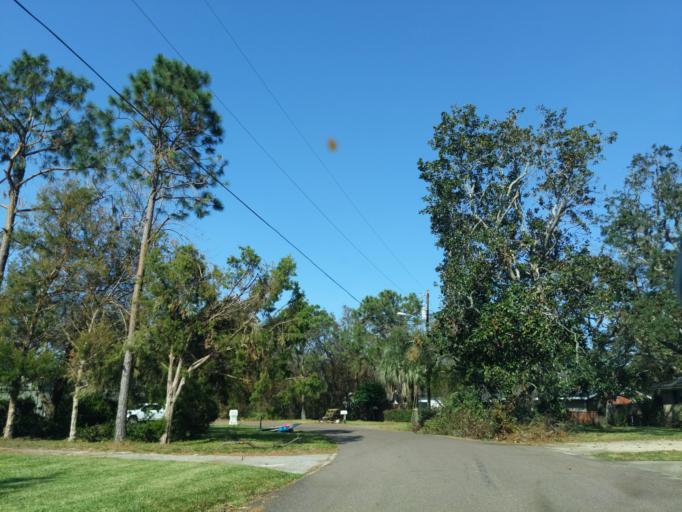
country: US
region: Florida
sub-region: Santa Rosa County
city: Gulf Breeze
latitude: 30.3599
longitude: -87.1800
